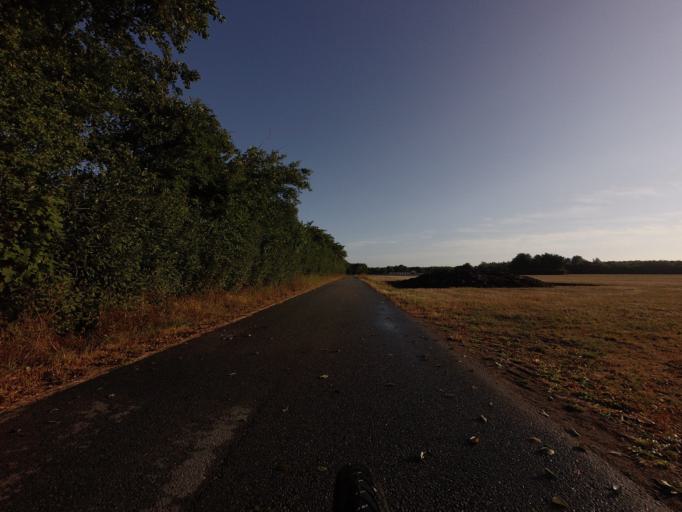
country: DK
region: North Denmark
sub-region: Hjorring Kommune
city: Vra
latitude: 57.3601
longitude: 9.8659
